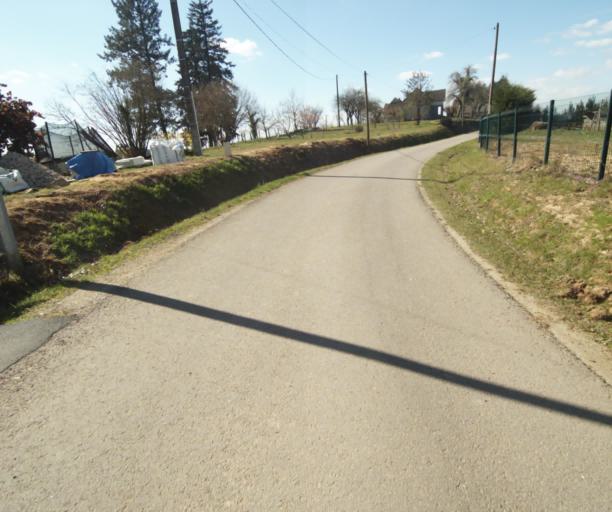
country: FR
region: Limousin
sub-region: Departement de la Correze
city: Saint-Mexant
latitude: 45.2909
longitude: 1.6817
